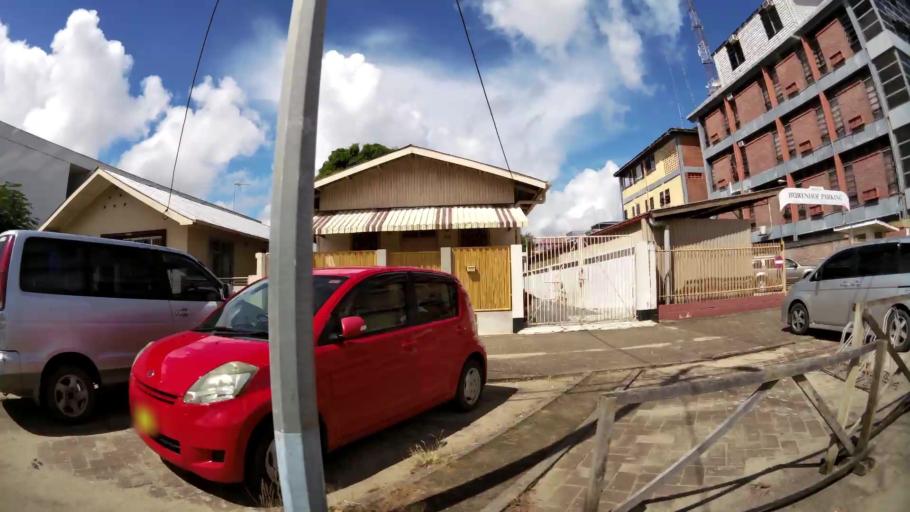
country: SR
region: Paramaribo
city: Paramaribo
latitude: 5.8275
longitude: -55.1640
